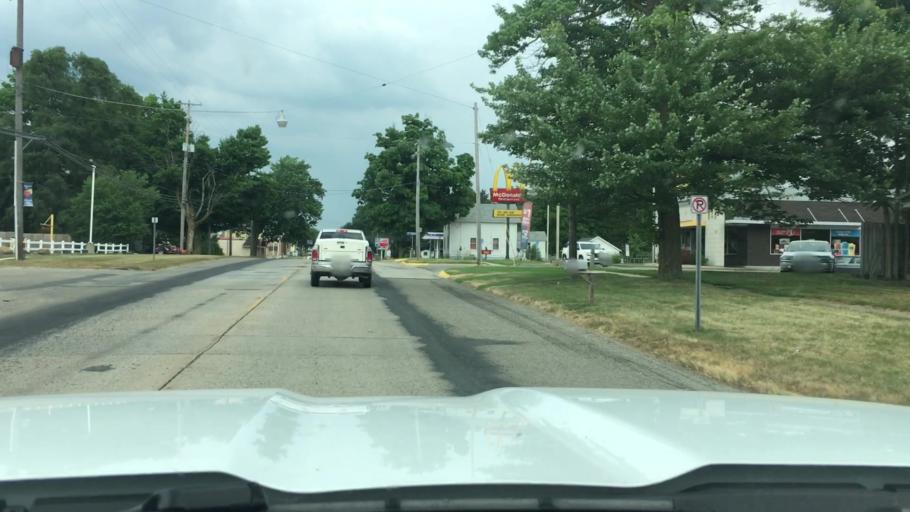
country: US
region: Michigan
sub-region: Montcalm County
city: Carson City
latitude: 43.1771
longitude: -84.8538
